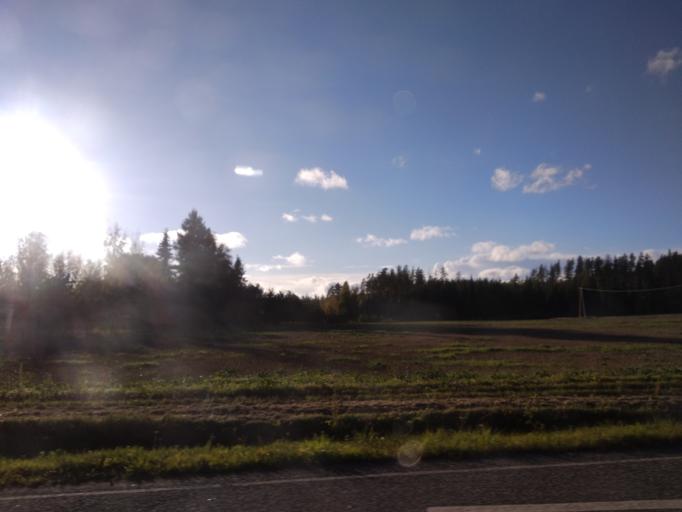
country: EE
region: Polvamaa
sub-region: Polva linn
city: Polva
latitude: 58.0325
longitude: 27.0661
